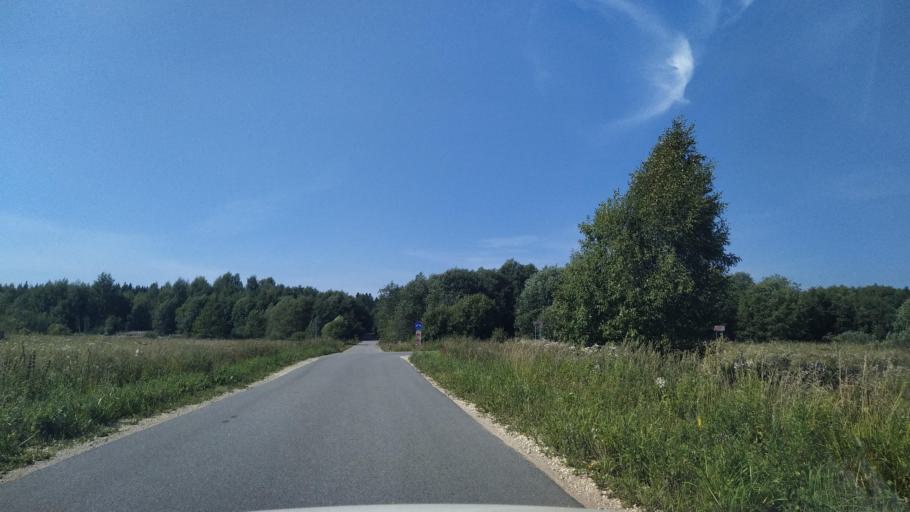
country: RU
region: Leningrad
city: Rozhdestveno
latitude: 59.2614
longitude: 30.0281
